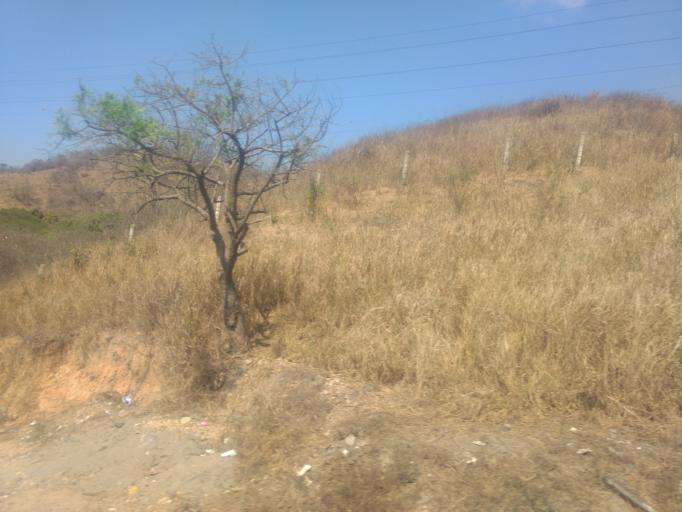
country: MX
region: Colima
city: El Colomo
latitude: 19.0614
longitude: -104.2699
